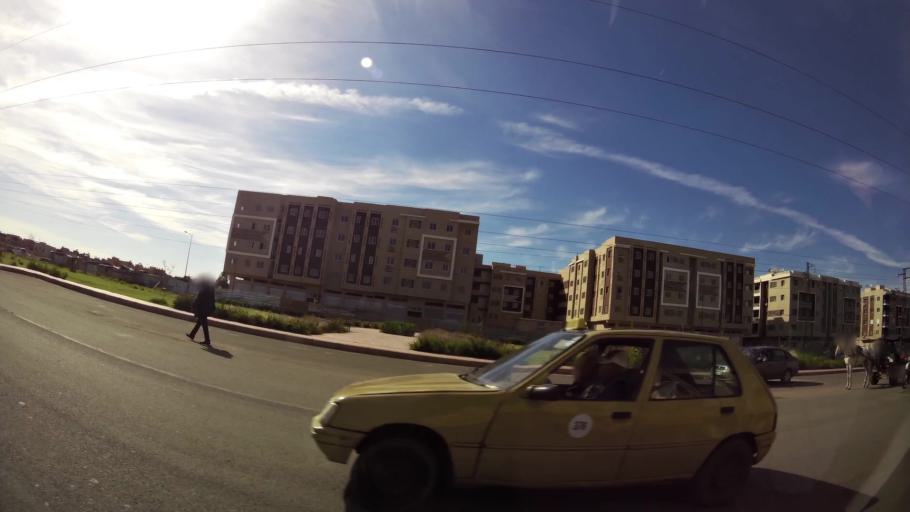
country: MA
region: Marrakech-Tensift-Al Haouz
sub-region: Marrakech
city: Marrakesh
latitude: 31.6469
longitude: -8.0375
